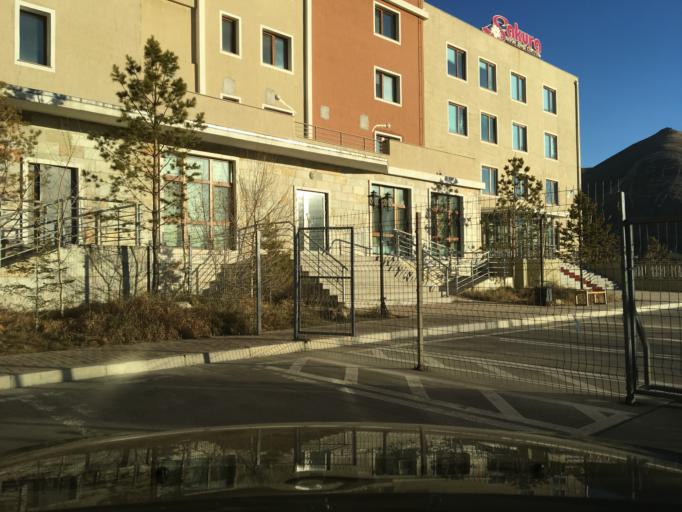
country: MN
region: Ulaanbaatar
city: Ulaanbaatar
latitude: 47.8902
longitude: 106.9237
